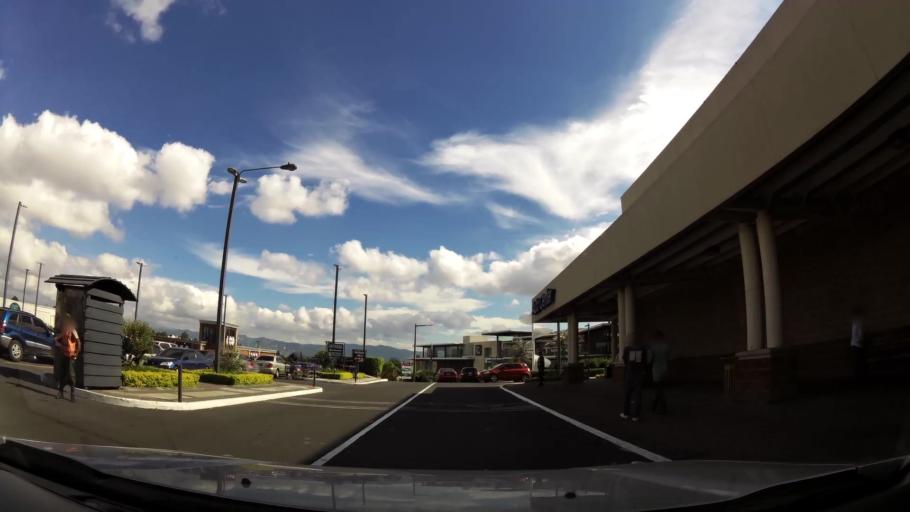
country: GT
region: Guatemala
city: Mixco
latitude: 14.6213
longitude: -90.5618
